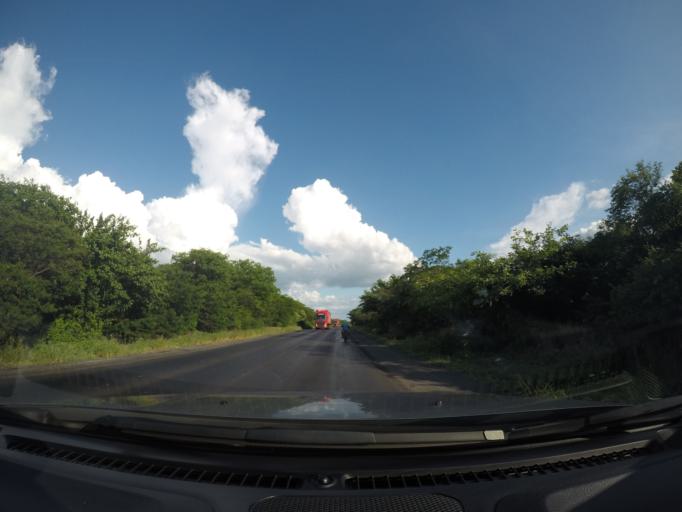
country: BR
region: Bahia
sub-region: Oliveira Dos Brejinhos
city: Oliveira dos Brejinhos
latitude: -12.0900
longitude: -42.9312
